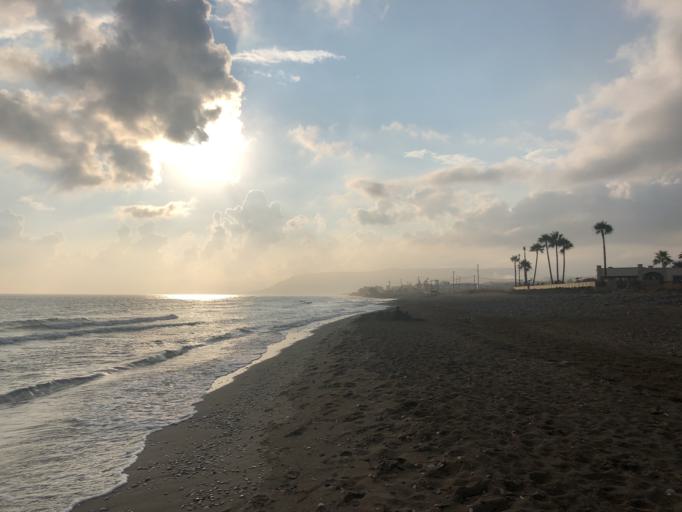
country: GR
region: Crete
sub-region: Nomos Chanias
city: Georgioupolis
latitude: 35.3533
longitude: 24.3022
